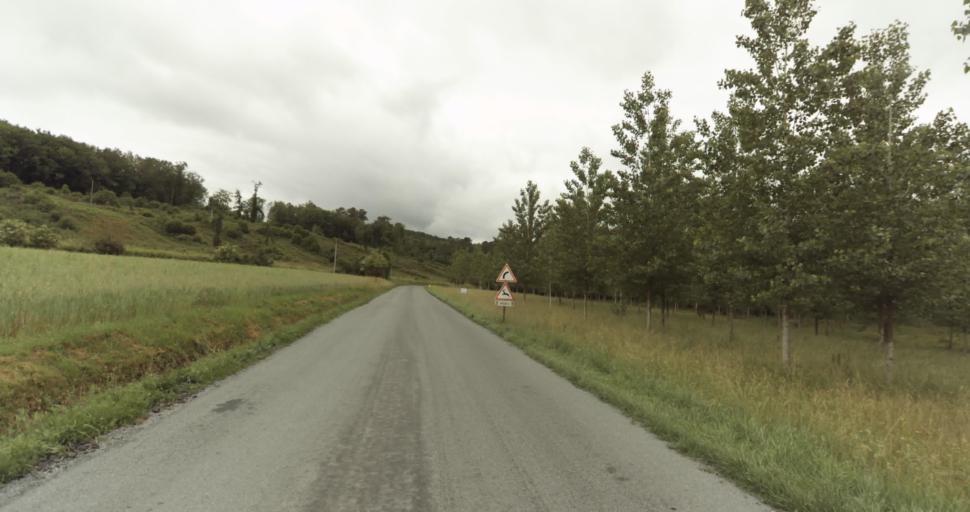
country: FR
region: Aquitaine
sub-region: Departement du Lot-et-Garonne
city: Villereal
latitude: 44.6547
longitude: 0.8590
